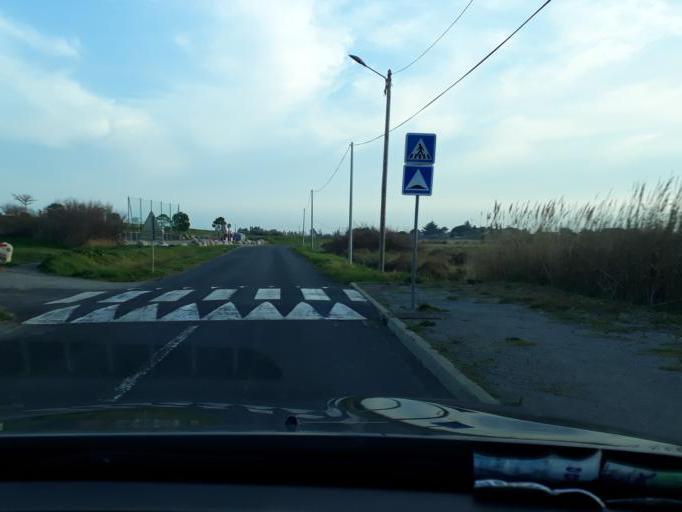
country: FR
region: Languedoc-Roussillon
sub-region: Departement de l'Herault
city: Marseillan
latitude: 43.3350
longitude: 3.5314
